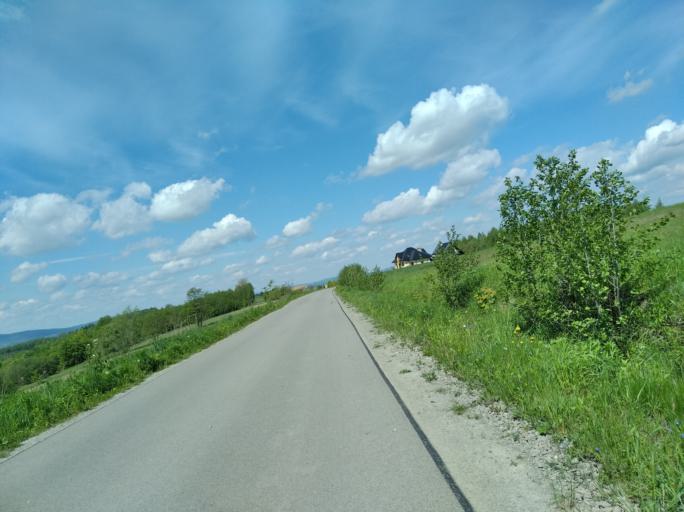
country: PL
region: Subcarpathian Voivodeship
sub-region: Powiat jasielski
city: Kolaczyce
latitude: 49.8384
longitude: 21.5001
